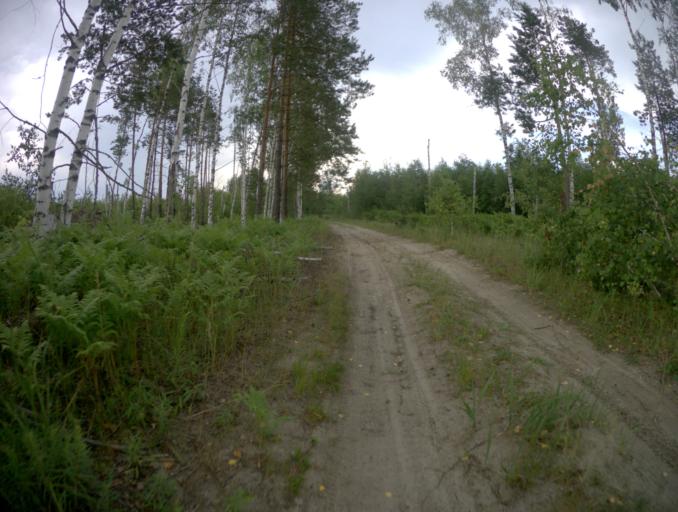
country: RU
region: Ivanovo
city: Talitsy
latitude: 56.5660
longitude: 42.4990
